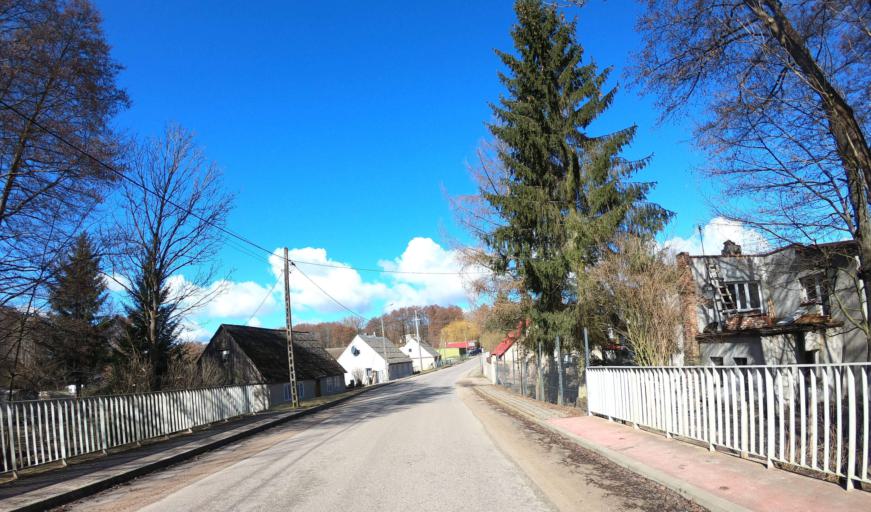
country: PL
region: West Pomeranian Voivodeship
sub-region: Powiat drawski
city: Zlocieniec
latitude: 53.4593
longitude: 15.9434
